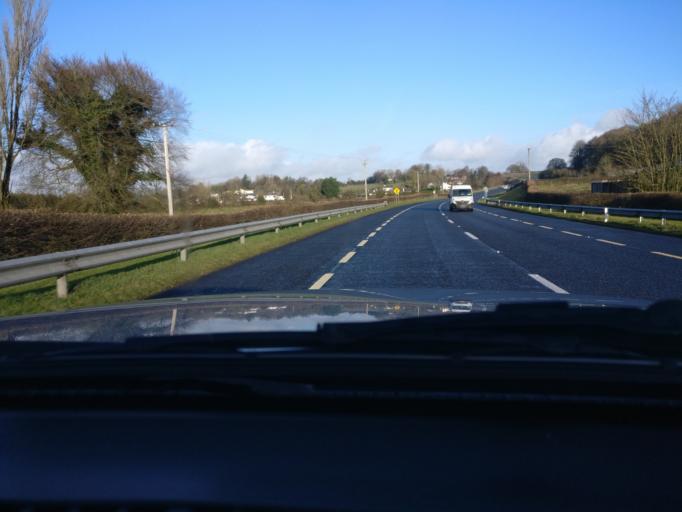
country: IE
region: Leinster
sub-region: An Iarmhi
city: An Muileann gCearr
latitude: 53.5427
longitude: -7.2994
